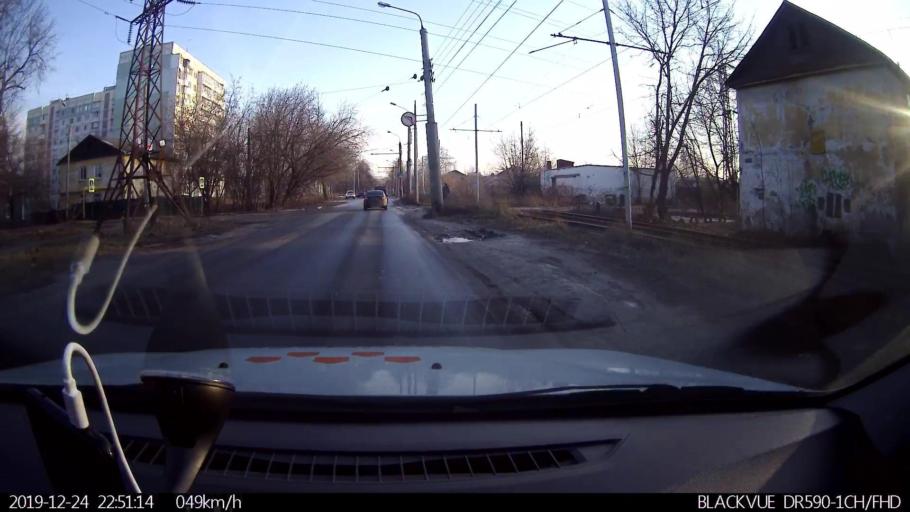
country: RU
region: Nizjnij Novgorod
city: Nizhniy Novgorod
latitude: 56.2887
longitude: 43.9079
